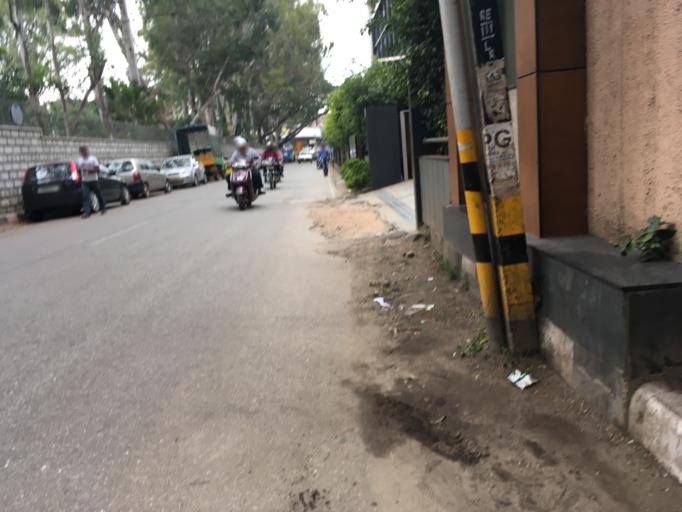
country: IN
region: Karnataka
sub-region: Bangalore Urban
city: Bangalore
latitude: 12.9666
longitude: 77.5965
